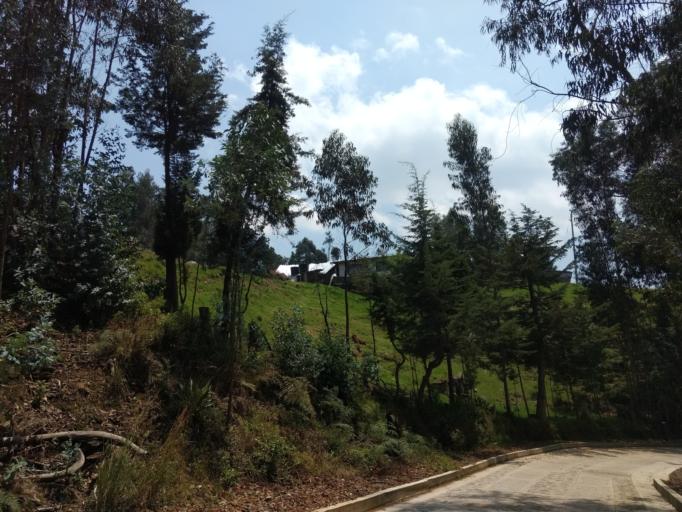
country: CO
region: Boyaca
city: Raquira
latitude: 5.5061
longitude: -73.7157
